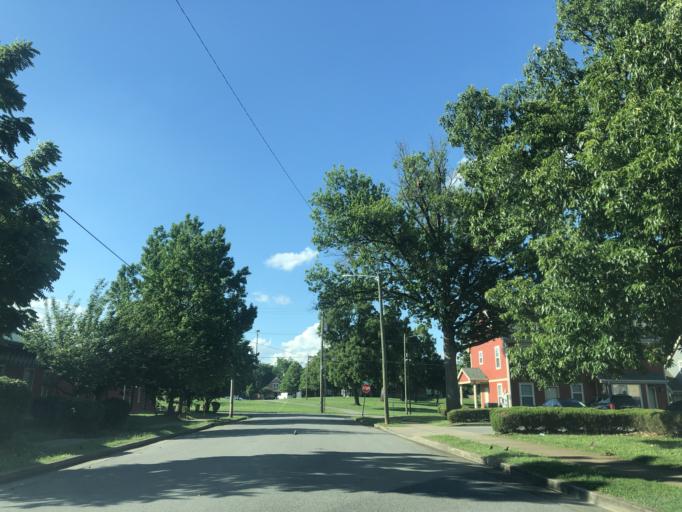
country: US
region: Tennessee
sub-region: Davidson County
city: Nashville
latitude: 36.1804
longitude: -86.7677
